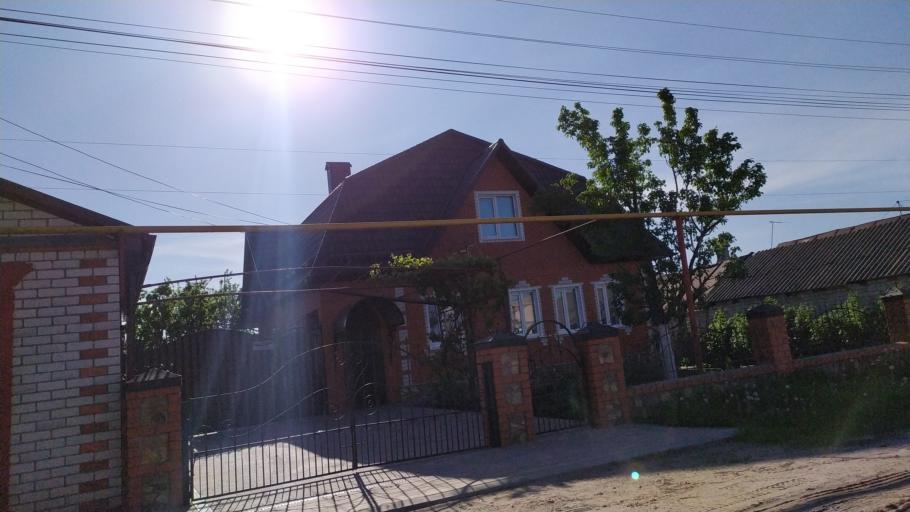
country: RU
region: Kursk
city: Kursk
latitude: 51.6390
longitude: 36.1484
